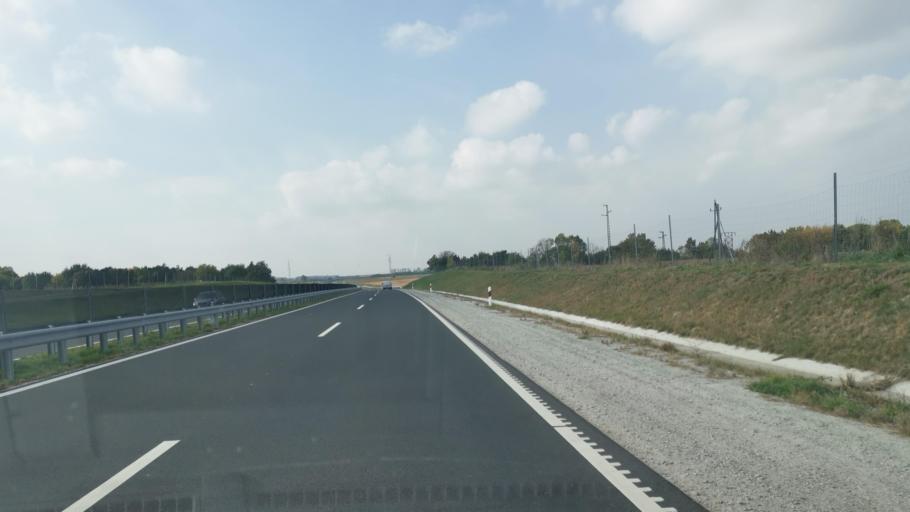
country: HU
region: Gyor-Moson-Sopron
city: Nagycenk
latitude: 47.5818
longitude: 16.7440
